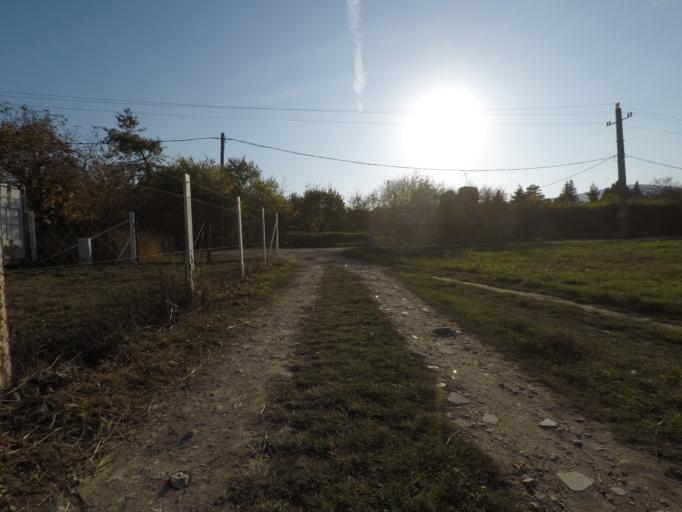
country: HU
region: Pest
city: Pomaz
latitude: 47.6290
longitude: 19.0331
